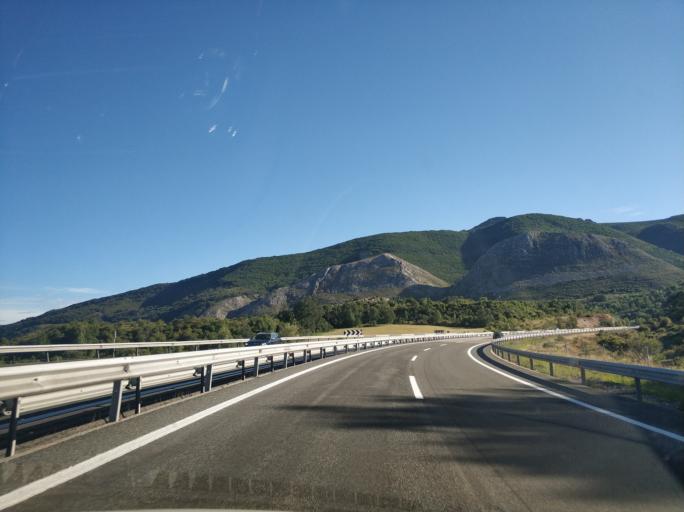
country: ES
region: Castille and Leon
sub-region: Provincia de Leon
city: Sena de Luna
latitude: 42.8769
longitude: -5.8810
